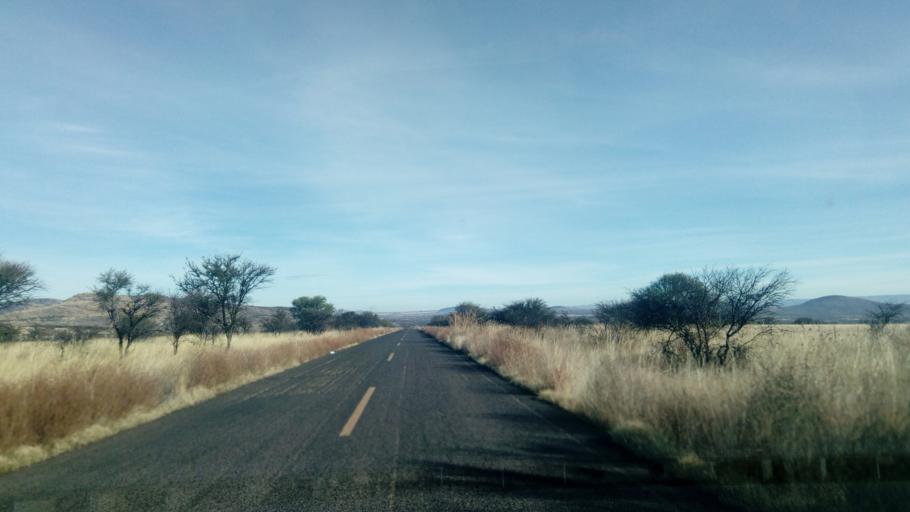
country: MX
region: Durango
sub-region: Nombre de Dios
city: Nombre de Dios
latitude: 23.9285
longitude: -104.3335
